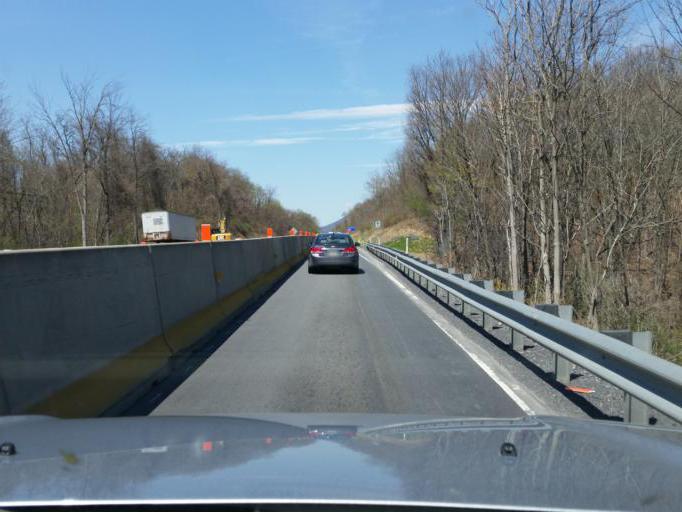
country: US
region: Pennsylvania
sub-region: Mifflin County
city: Lewistown
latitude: 40.5859
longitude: -77.5555
